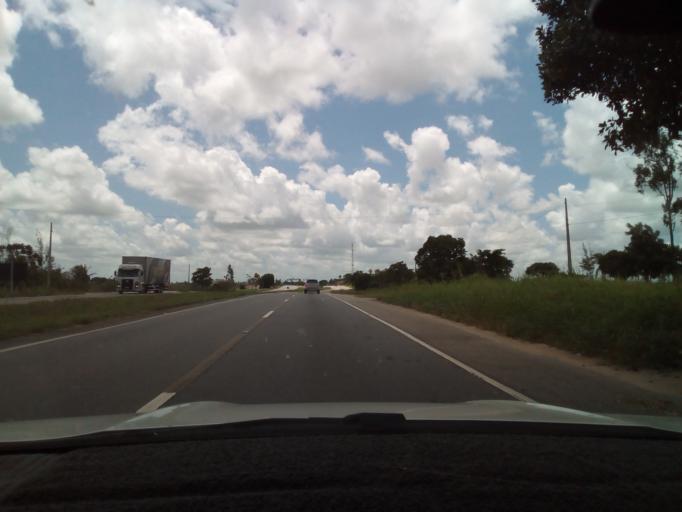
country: BR
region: Paraiba
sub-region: Pilar
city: Pilar
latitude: -7.1910
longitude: -35.2401
